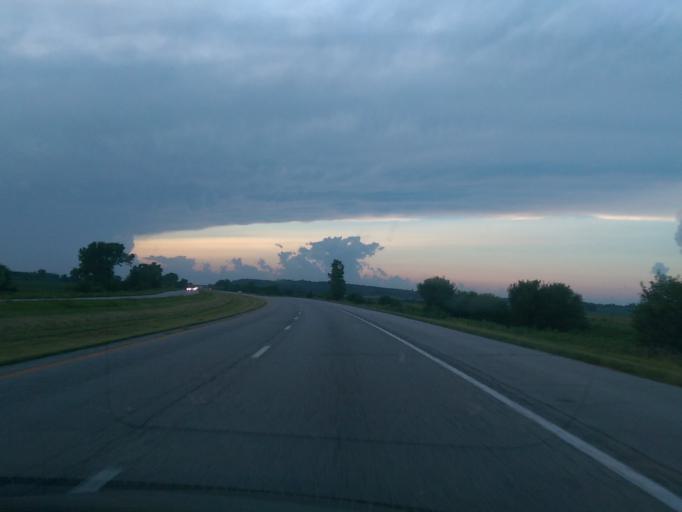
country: US
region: Iowa
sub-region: Fremont County
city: Hamburg
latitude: 40.5170
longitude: -95.6032
